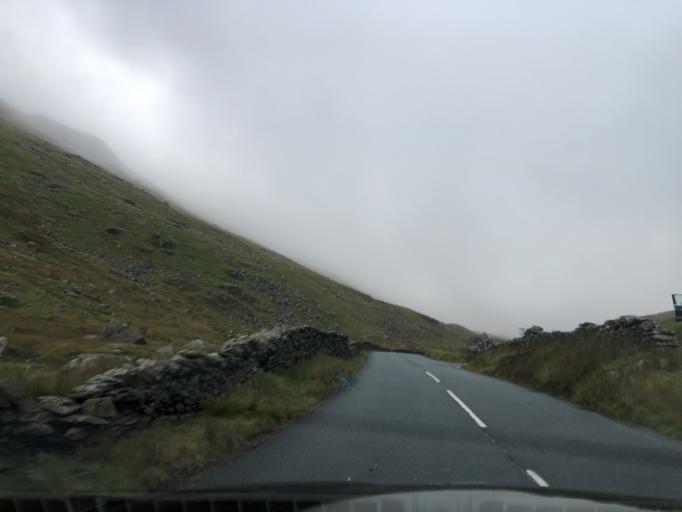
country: GB
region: England
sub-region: Cumbria
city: Ambleside
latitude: 54.4726
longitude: -2.9228
